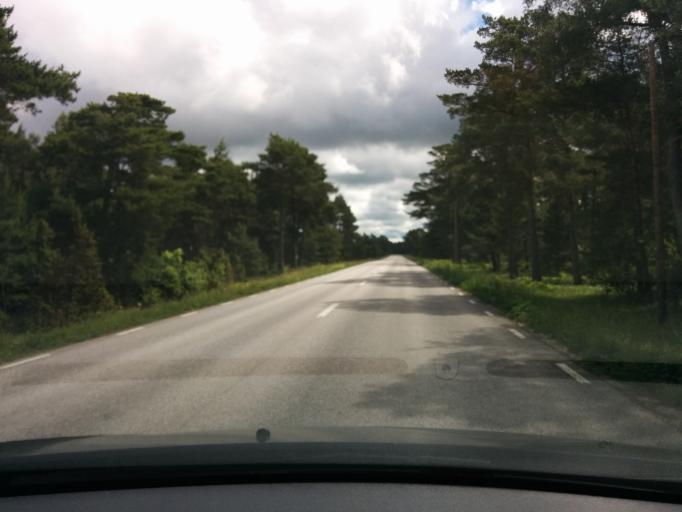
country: SE
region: Gotland
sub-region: Gotland
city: Visby
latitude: 57.6382
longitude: 18.3887
